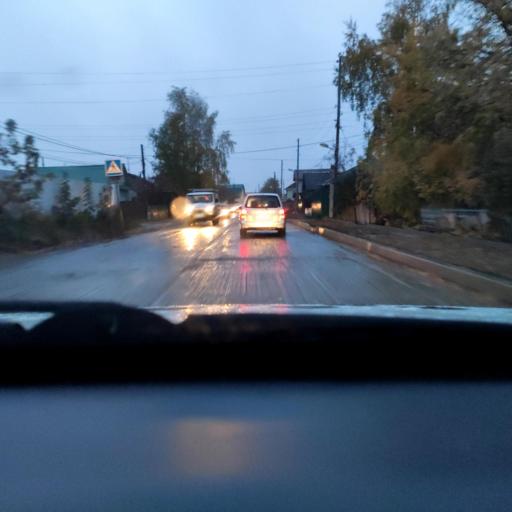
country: RU
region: Perm
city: Kondratovo
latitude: 57.9600
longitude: 56.1268
